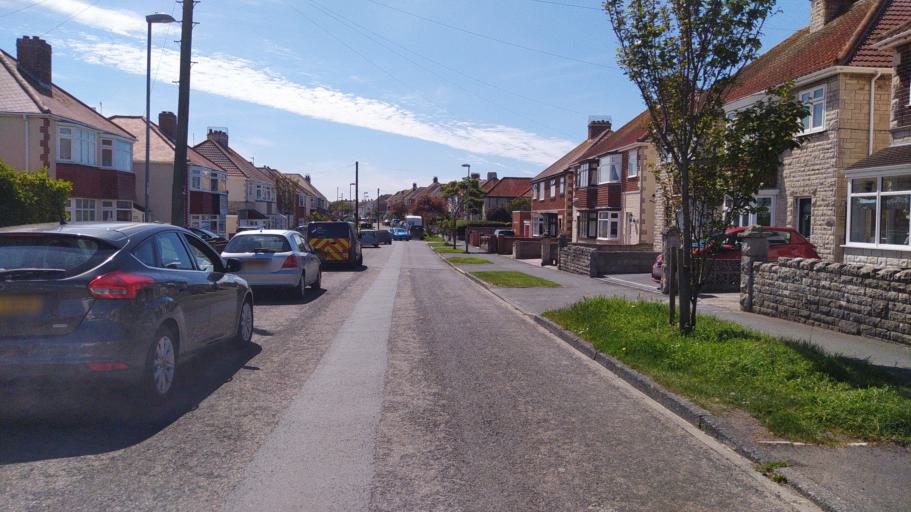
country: GB
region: England
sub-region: Dorset
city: Weymouth
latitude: 50.5914
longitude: -2.4766
